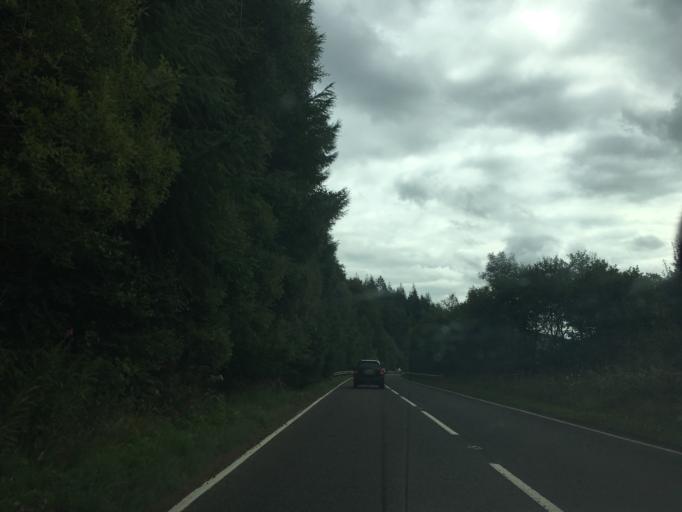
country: GB
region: Scotland
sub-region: Stirling
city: Callander
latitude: 56.2997
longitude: -4.3071
